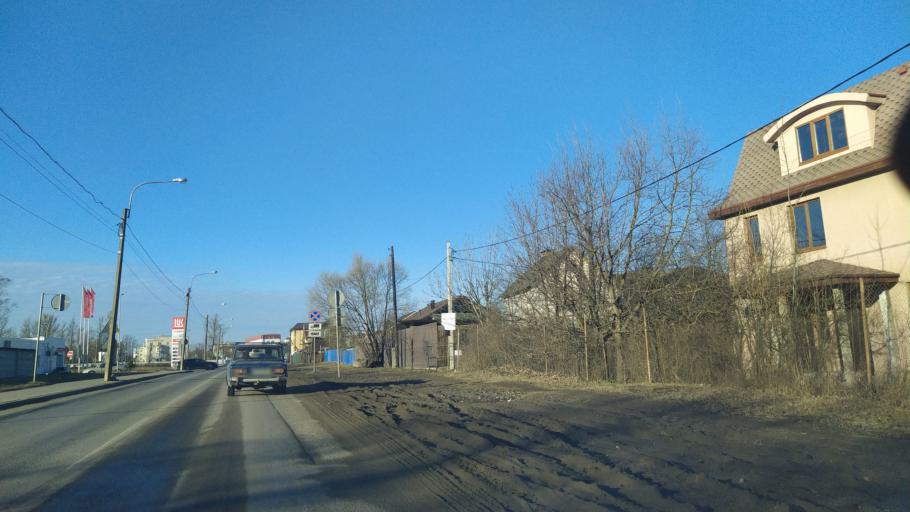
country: RU
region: St.-Petersburg
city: Pushkin
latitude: 59.6984
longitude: 30.3948
